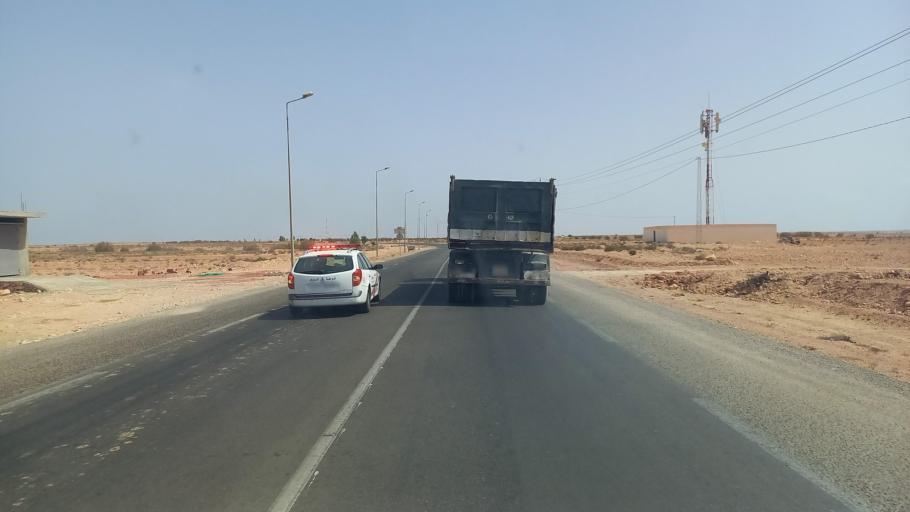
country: TN
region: Madanin
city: Medenine
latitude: 33.3753
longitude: 10.6948
